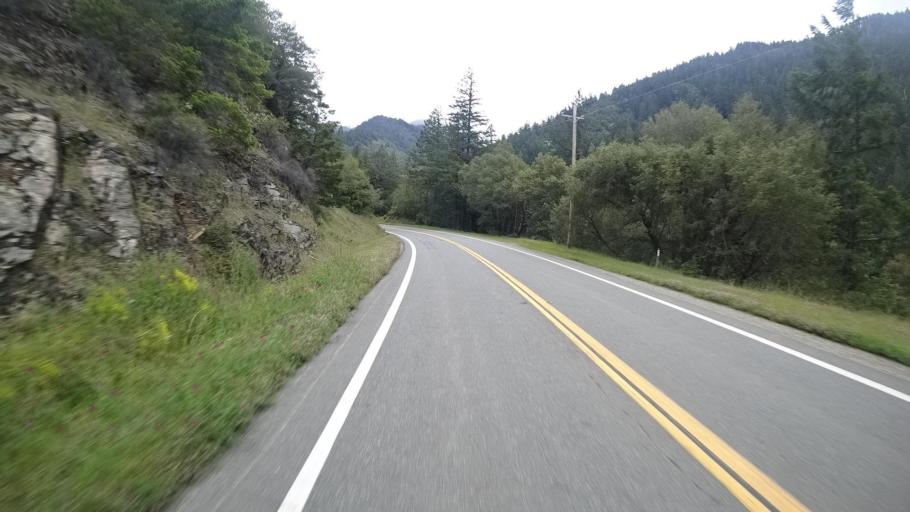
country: US
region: California
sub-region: Humboldt County
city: Willow Creek
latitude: 41.1999
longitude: -123.6653
